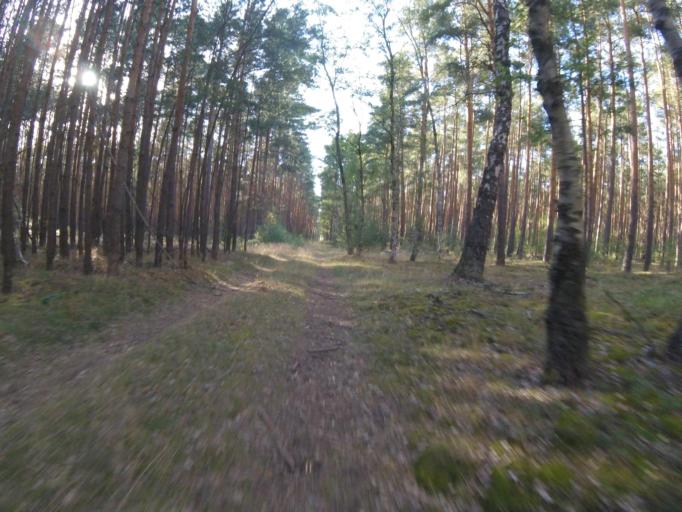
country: DE
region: Berlin
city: Schmockwitz
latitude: 52.3385
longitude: 13.6977
